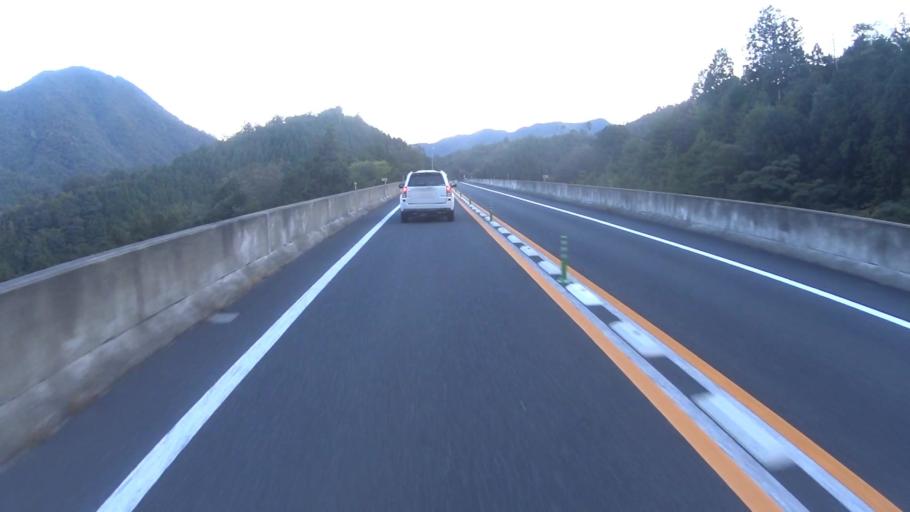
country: JP
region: Kyoto
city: Miyazu
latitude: 35.4565
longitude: 135.1781
